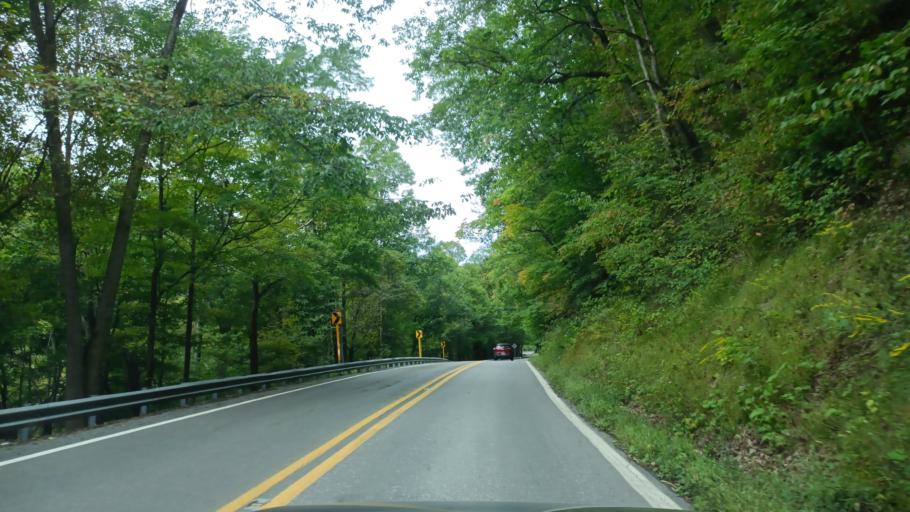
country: US
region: West Virginia
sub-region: Preston County
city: Kingwood
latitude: 39.3308
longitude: -79.7271
